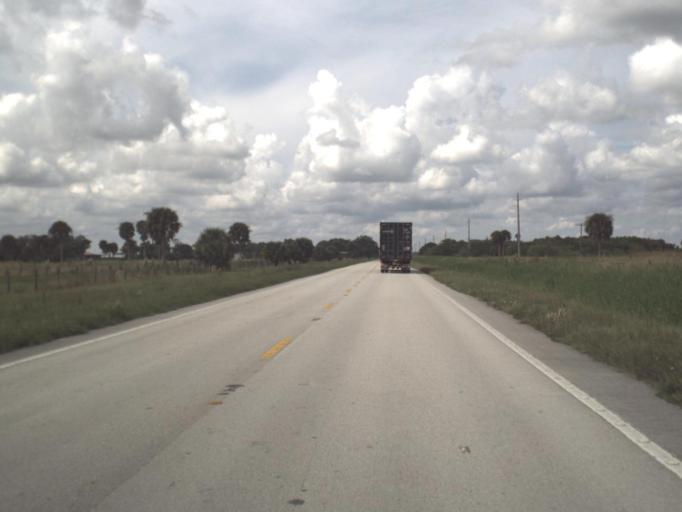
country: US
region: Florida
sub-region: Okeechobee County
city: Okeechobee
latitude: 27.2436
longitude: -80.9489
